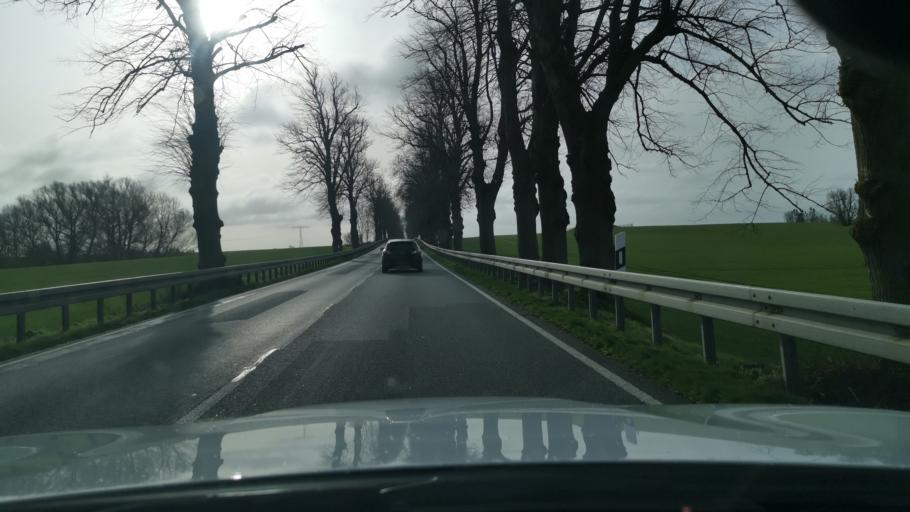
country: DE
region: Mecklenburg-Vorpommern
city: Laage
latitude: 53.9499
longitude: 12.3058
